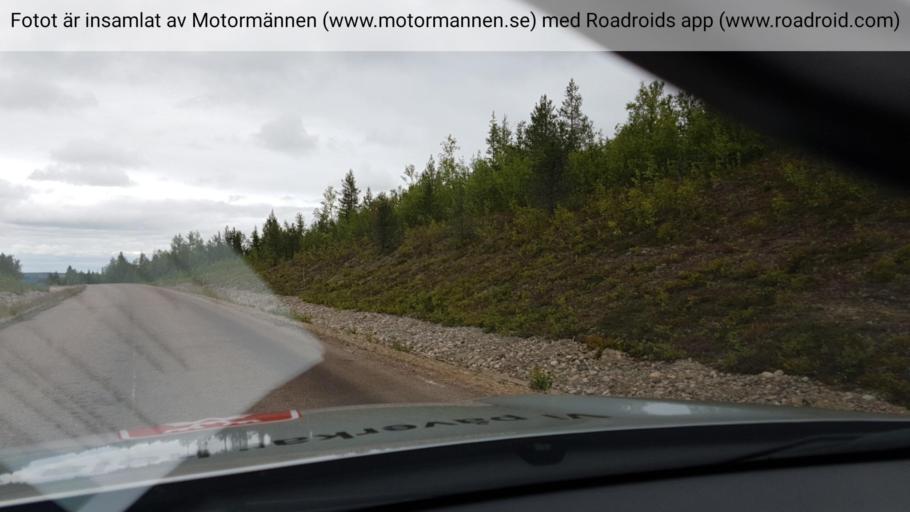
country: SE
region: Norrbotten
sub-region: Overkalix Kommun
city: OEverkalix
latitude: 67.0436
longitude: 22.1336
